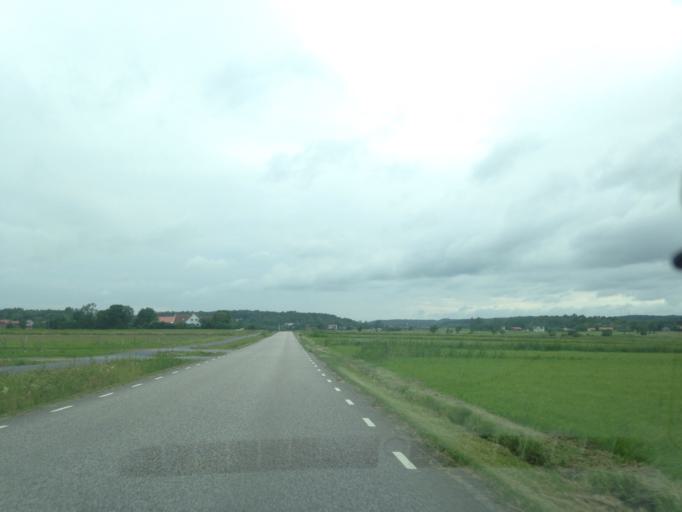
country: SE
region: Vaestra Goetaland
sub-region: Goteborg
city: Torslanda
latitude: 57.8181
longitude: 11.8366
